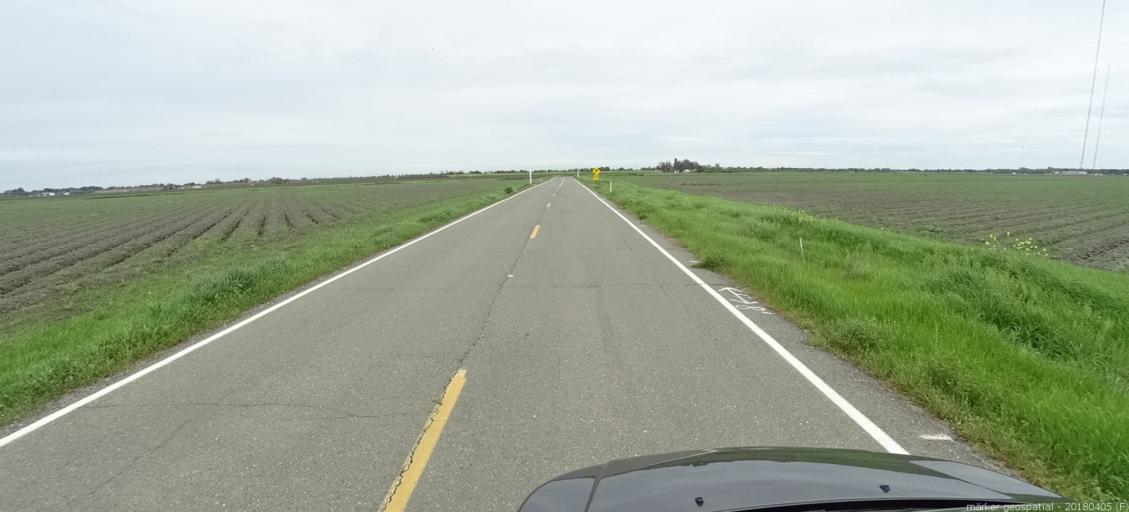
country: US
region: California
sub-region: Sacramento County
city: Walnut Grove
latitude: 38.2836
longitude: -121.5289
